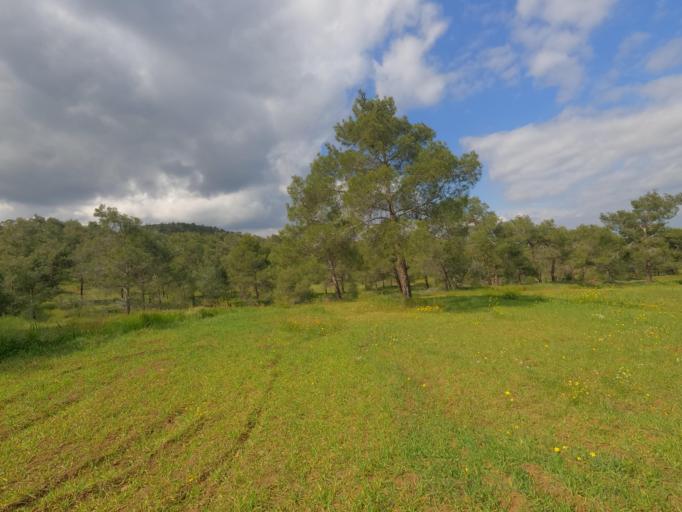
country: CY
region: Lefkosia
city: Astromeritis
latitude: 35.0721
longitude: 32.9643
